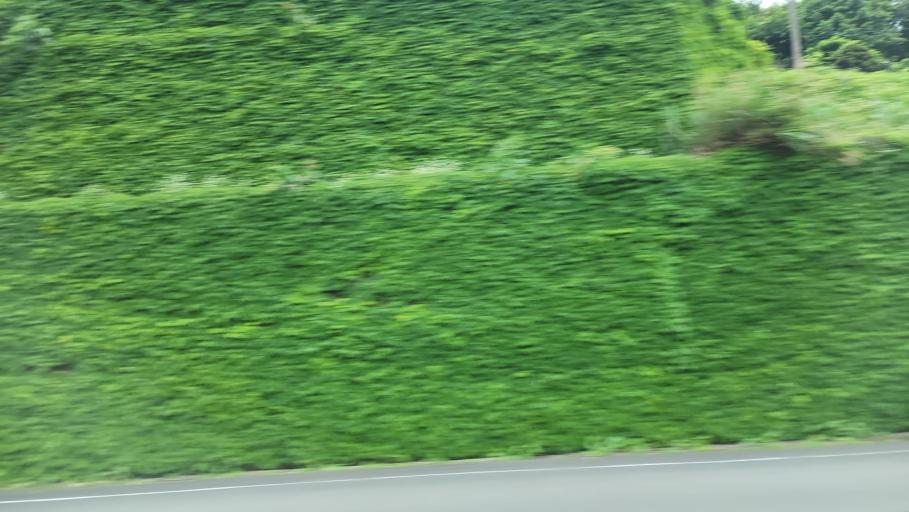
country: TW
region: Taiwan
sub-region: Keelung
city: Keelung
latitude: 25.1948
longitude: 121.6812
